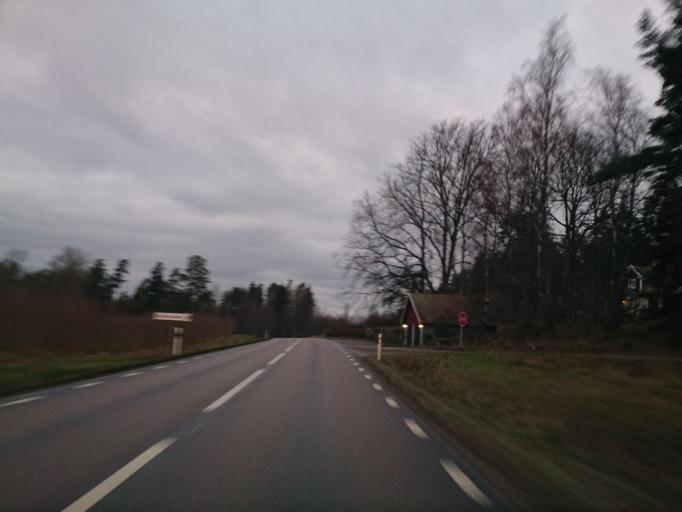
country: SE
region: OEstergoetland
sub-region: Atvidabergs Kommun
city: Atvidaberg
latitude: 58.3043
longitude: 15.8868
